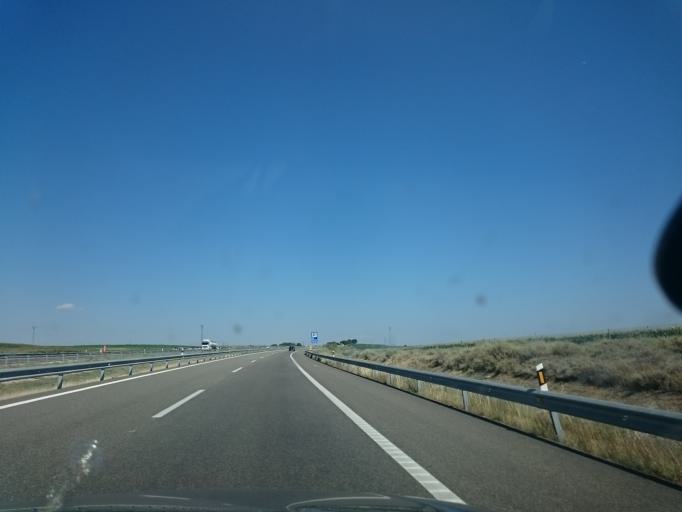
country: ES
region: Aragon
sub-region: Provincia de Huesca
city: Valfarta
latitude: 41.5196
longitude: -0.1098
